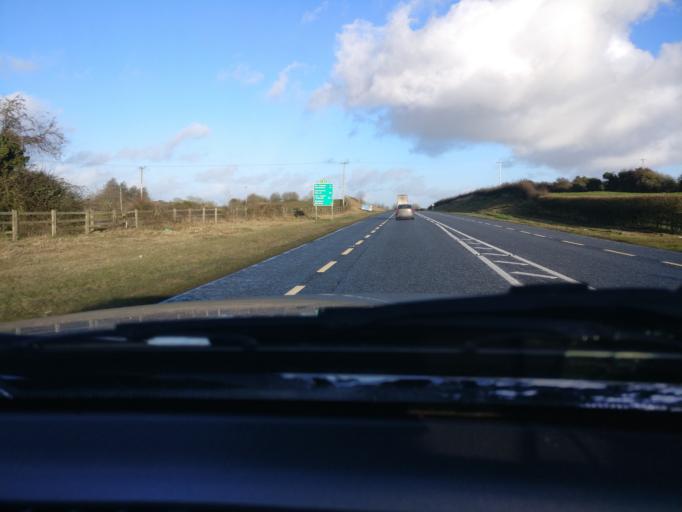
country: IE
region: Leinster
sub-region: An Iarmhi
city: Rathwire
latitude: 53.5969
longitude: -7.1113
